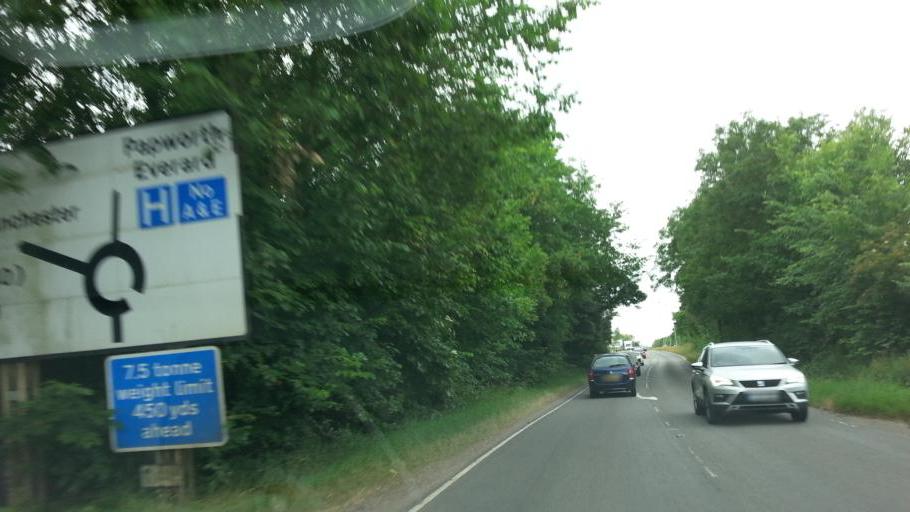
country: GB
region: England
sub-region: Cambridgeshire
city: Papworth Everard
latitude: 52.2394
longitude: -0.1110
